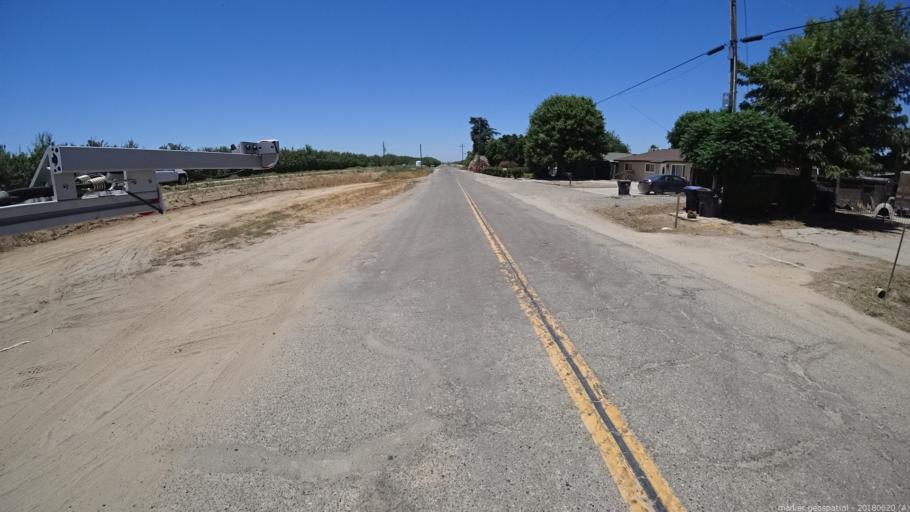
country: US
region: California
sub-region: Fresno County
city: Biola
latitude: 36.8658
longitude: -119.9634
